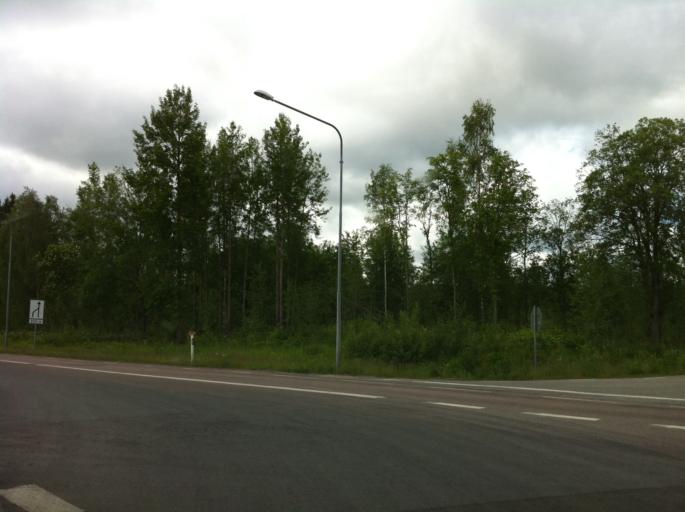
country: SE
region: Vaermland
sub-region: Sunne Kommun
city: Sunne
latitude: 59.8374
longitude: 13.1269
